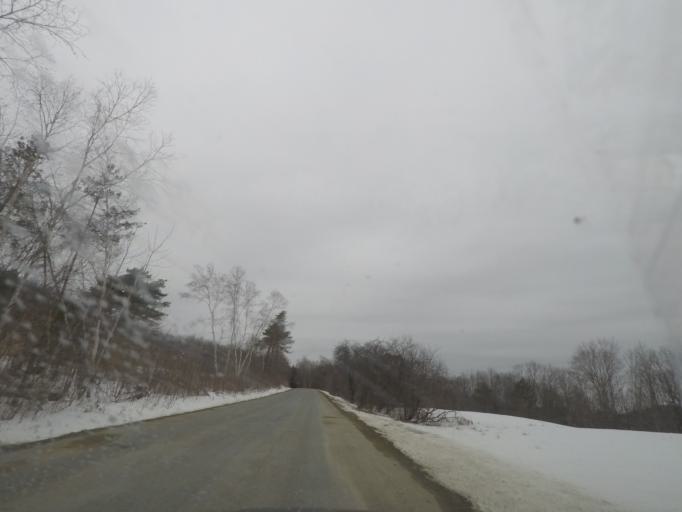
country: US
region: New York
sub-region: Rensselaer County
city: Averill Park
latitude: 42.5600
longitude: -73.4126
